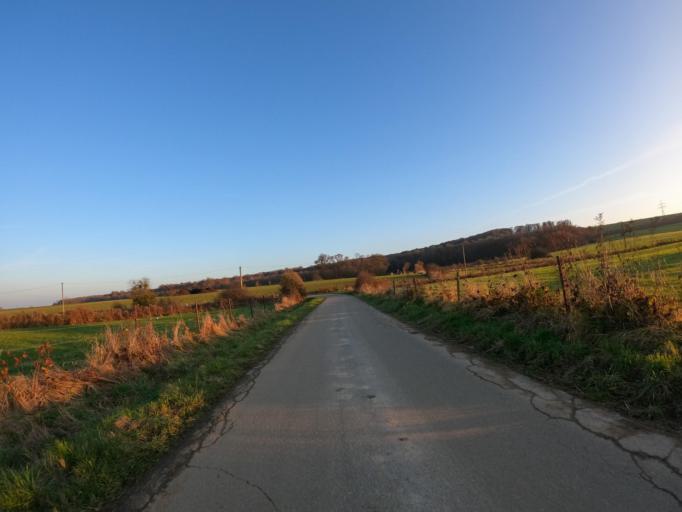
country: LU
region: Luxembourg
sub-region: Canton de Luxembourg
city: Bertrange
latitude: 49.5904
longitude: 6.0319
